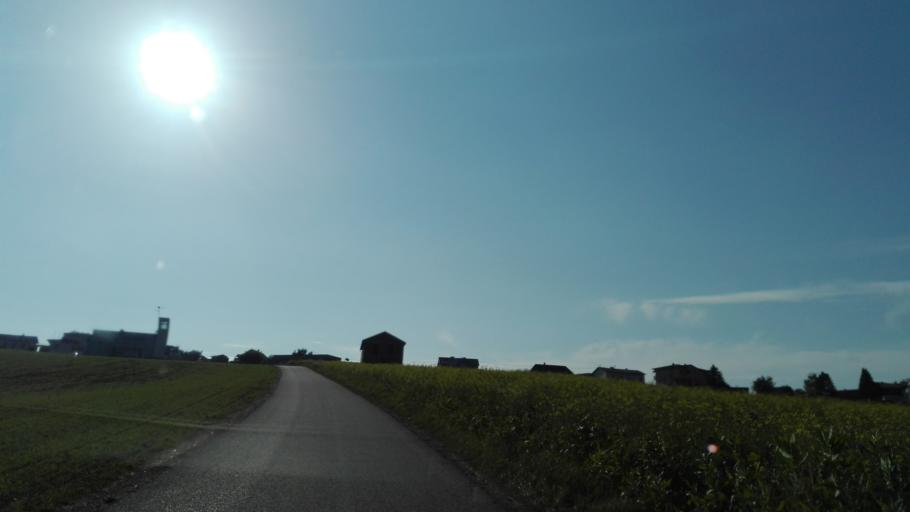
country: AT
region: Upper Austria
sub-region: Politischer Bezirk Perg
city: Perg
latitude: 48.2886
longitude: 14.5959
